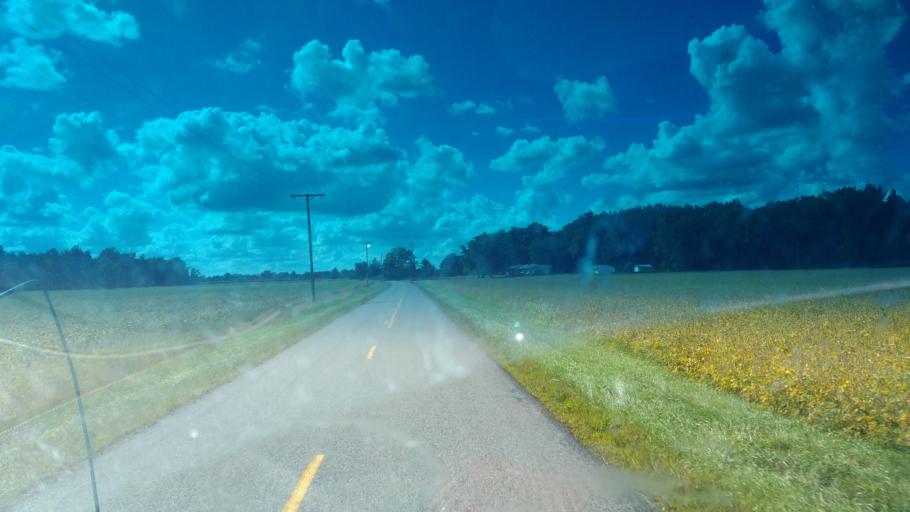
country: US
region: Ohio
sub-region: Hardin County
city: Kenton
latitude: 40.5183
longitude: -83.5495
